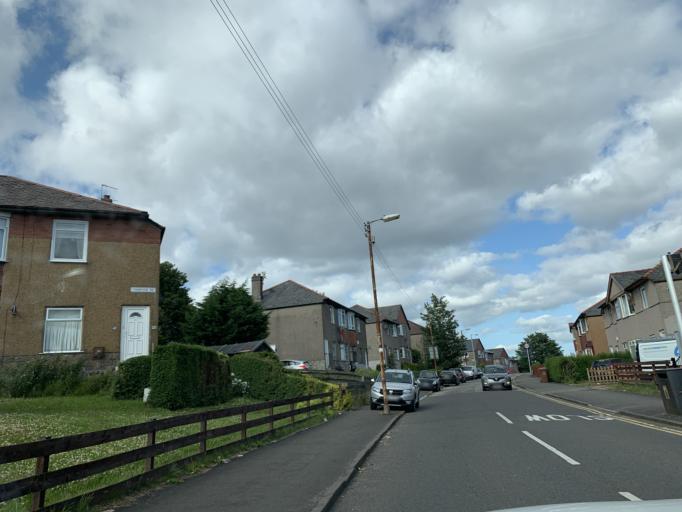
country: GB
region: Scotland
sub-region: Renfrewshire
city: Renfrew
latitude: 55.8513
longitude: -4.3567
